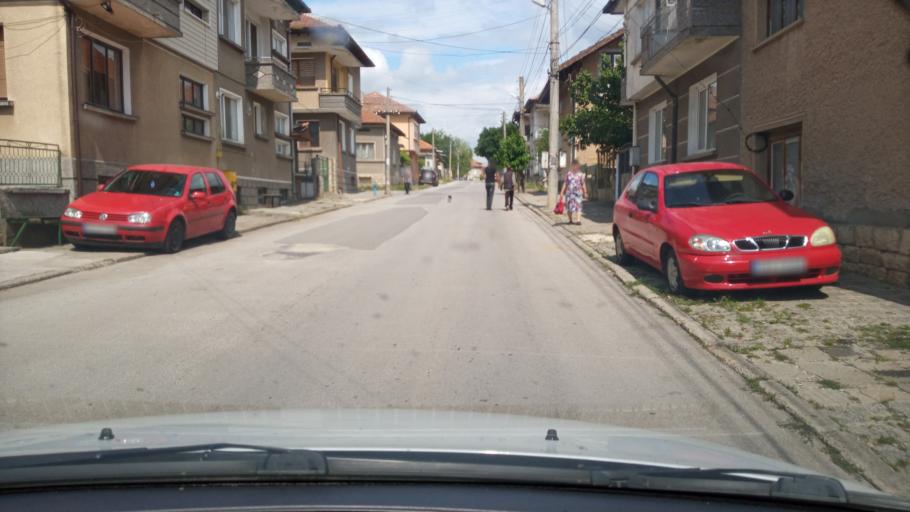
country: BG
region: Lovech
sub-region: Obshtina Lukovit
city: Lukovit
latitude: 43.2065
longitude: 24.1573
